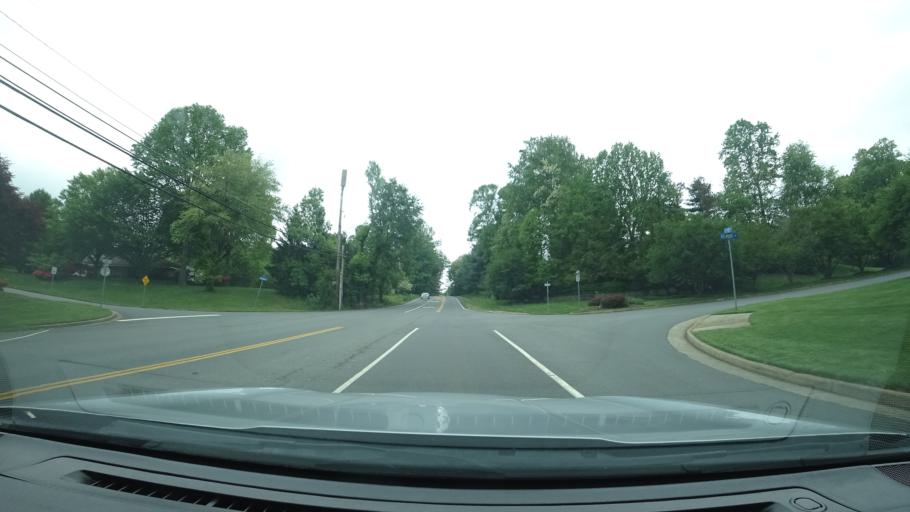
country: US
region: Virginia
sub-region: Fairfax County
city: Oakton
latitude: 38.8963
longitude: -77.3522
